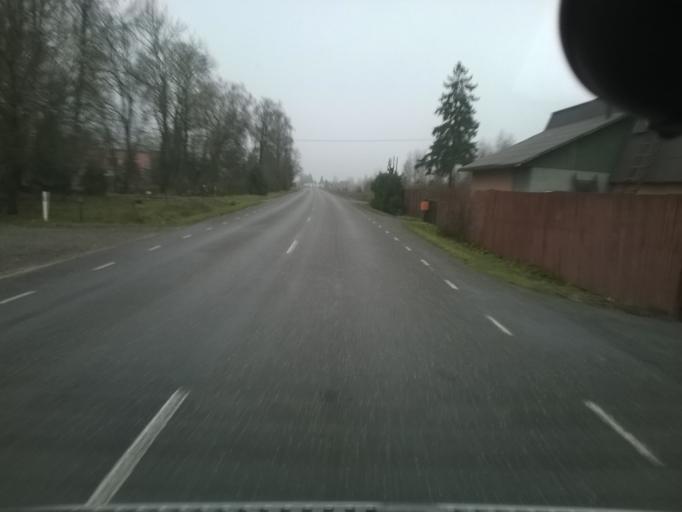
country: EE
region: Raplamaa
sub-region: Kohila vald
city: Kohila
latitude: 59.1559
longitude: 24.6301
